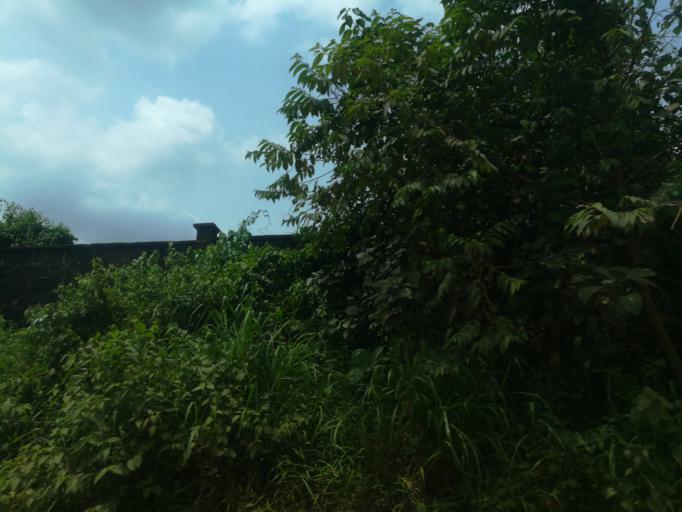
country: NG
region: Oyo
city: Moniya
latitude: 7.4650
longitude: 3.9545
